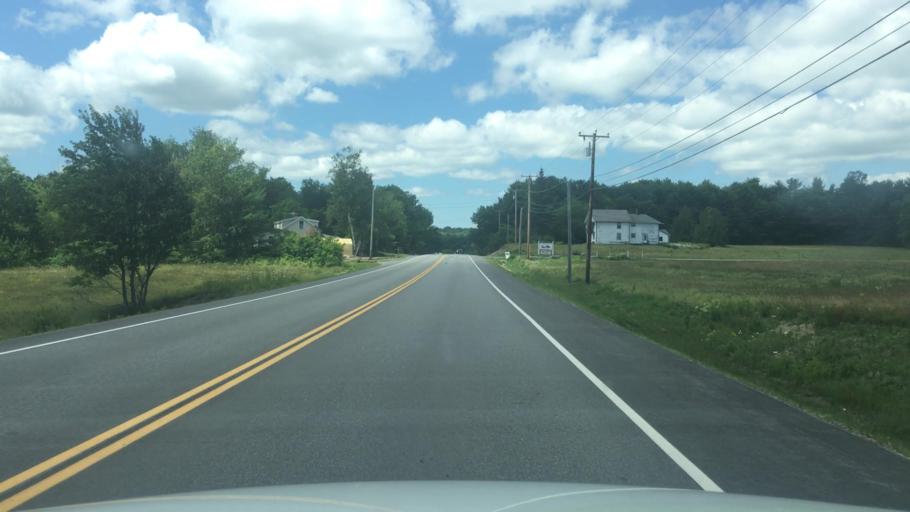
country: US
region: Maine
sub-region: Waldo County
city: Belfast
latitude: 44.4144
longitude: -69.0521
